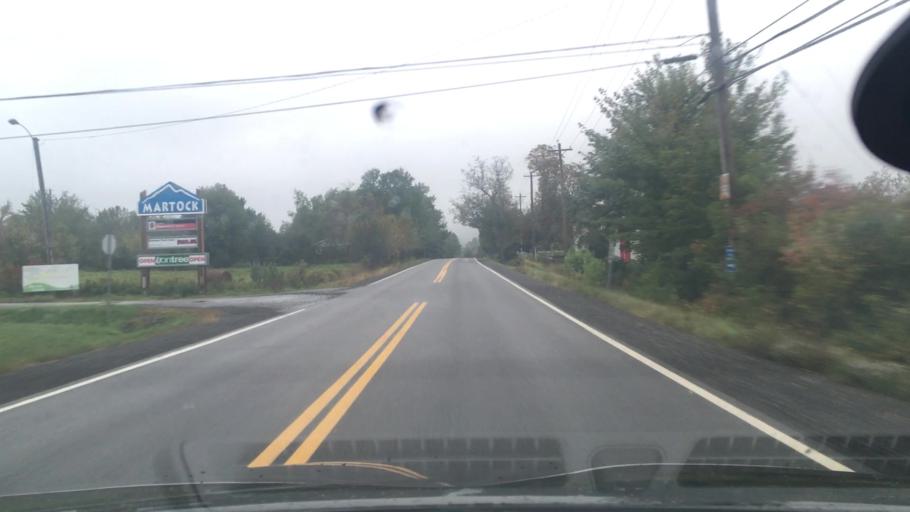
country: CA
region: Nova Scotia
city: Windsor
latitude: 44.9397
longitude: -64.1895
